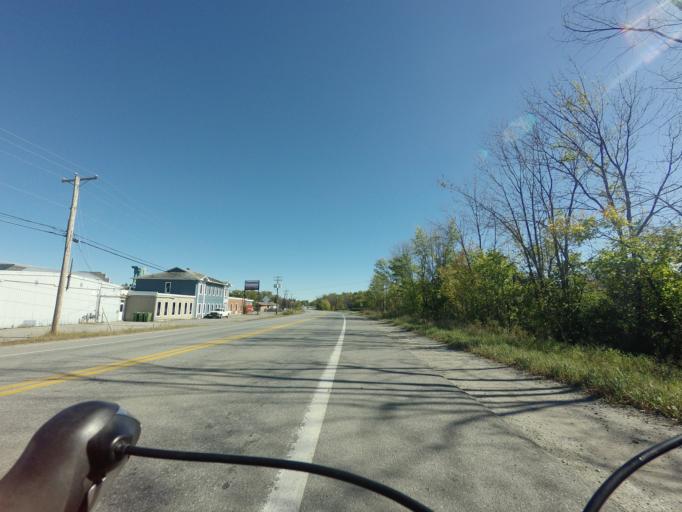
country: CA
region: Quebec
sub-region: Outaouais
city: Gatineau
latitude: 45.5144
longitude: -75.5268
